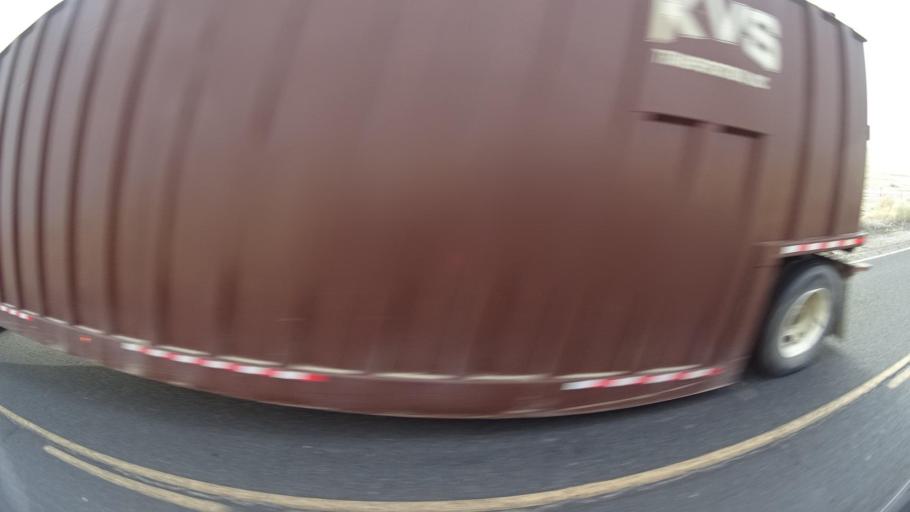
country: US
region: California
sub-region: Kern County
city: Ford City
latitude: 35.2378
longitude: -119.4479
